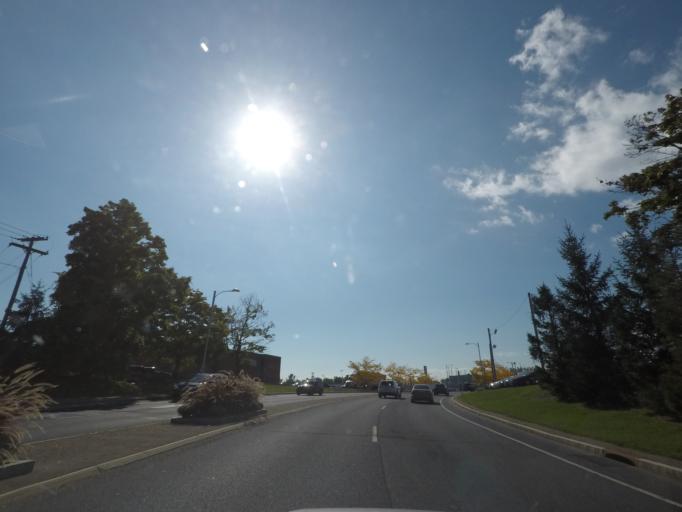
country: US
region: New York
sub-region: Albany County
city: West Albany
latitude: 42.6797
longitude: -73.7859
